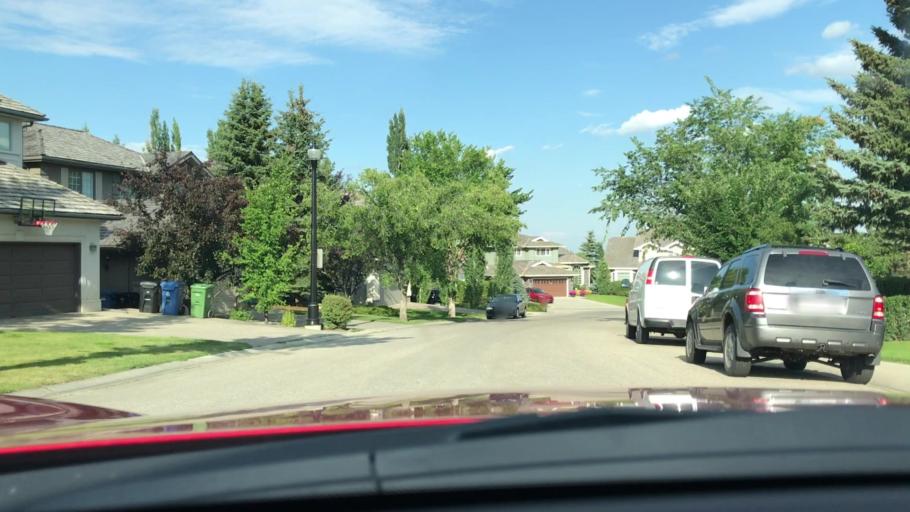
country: CA
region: Alberta
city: Calgary
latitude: 51.0265
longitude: -114.1727
